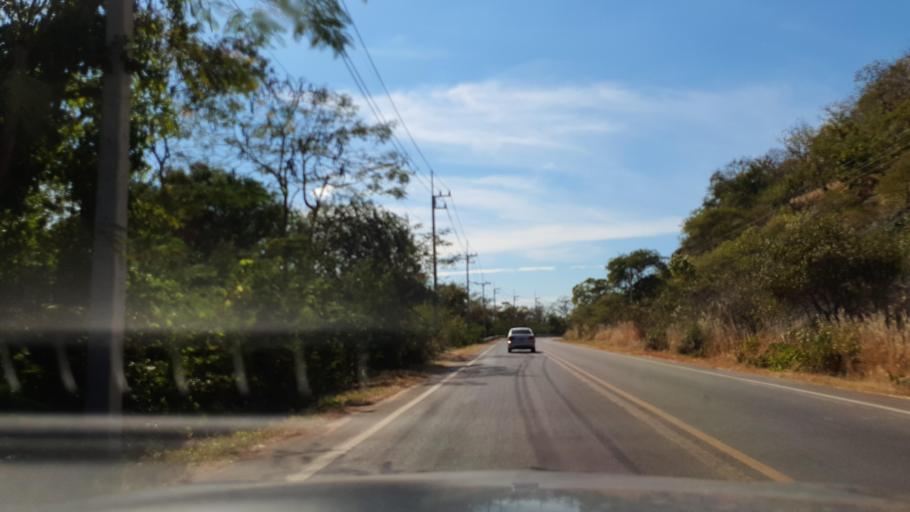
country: TH
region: Kalasin
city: Khao Wong
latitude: 16.7552
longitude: 104.1248
